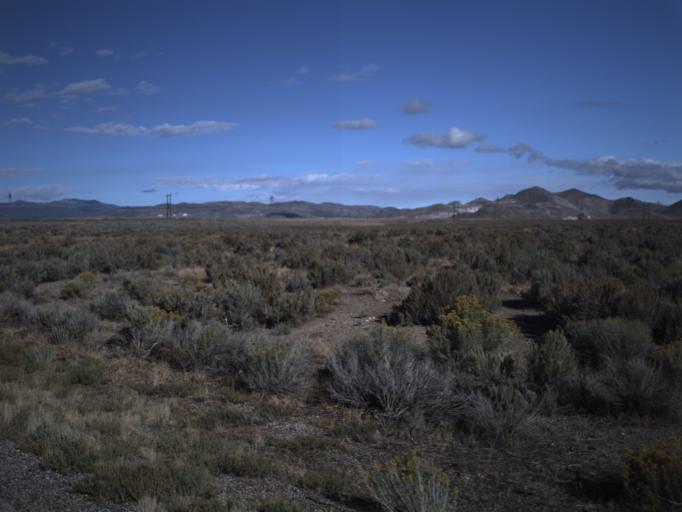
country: US
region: Utah
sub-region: Beaver County
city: Milford
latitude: 38.4064
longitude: -113.0505
